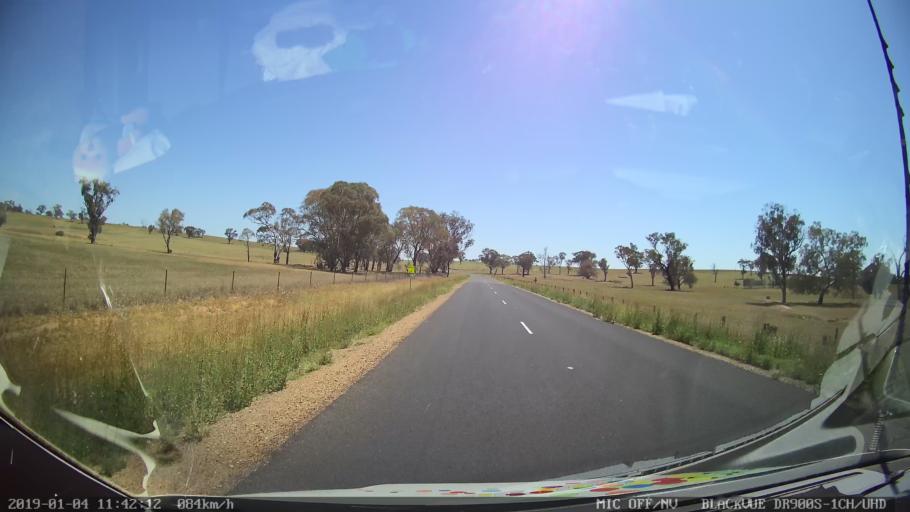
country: AU
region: New South Wales
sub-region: Cabonne
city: Molong
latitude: -32.9844
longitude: 148.7867
